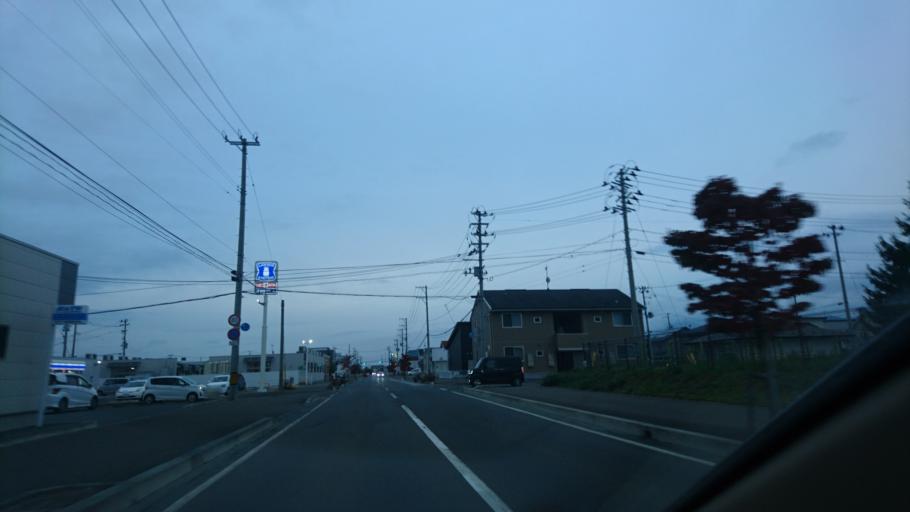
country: JP
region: Iwate
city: Morioka-shi
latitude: 39.6750
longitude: 141.1321
